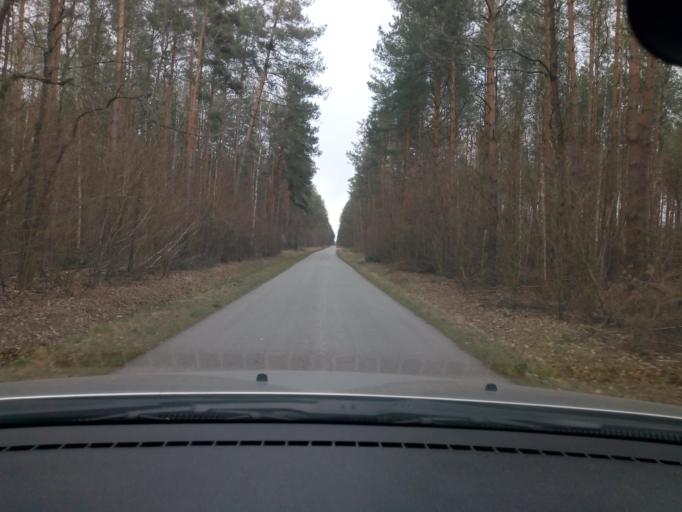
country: PL
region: Swietokrzyskie
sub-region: Powiat starachowicki
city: Brody
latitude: 51.0697
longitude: 21.3089
